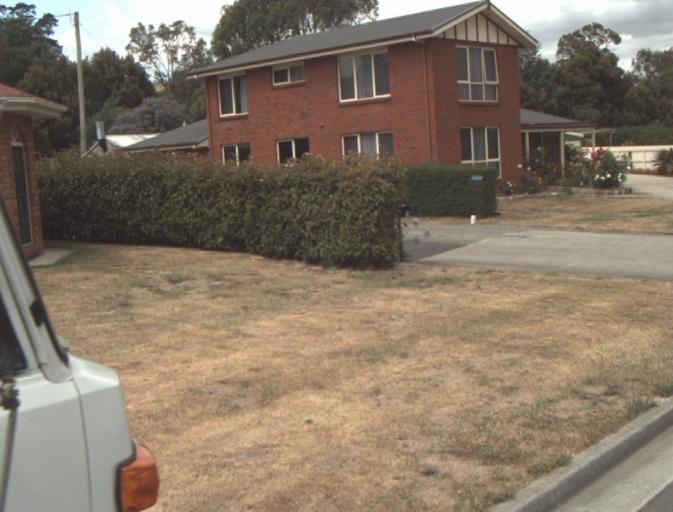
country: AU
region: Tasmania
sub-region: Launceston
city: Newstead
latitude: -41.4497
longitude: 147.1909
